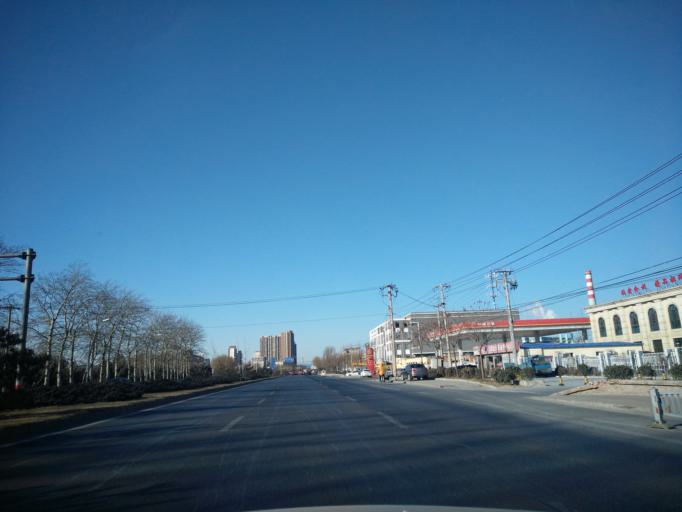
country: CN
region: Beijing
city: Xingfeng
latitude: 39.7206
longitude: 116.3522
